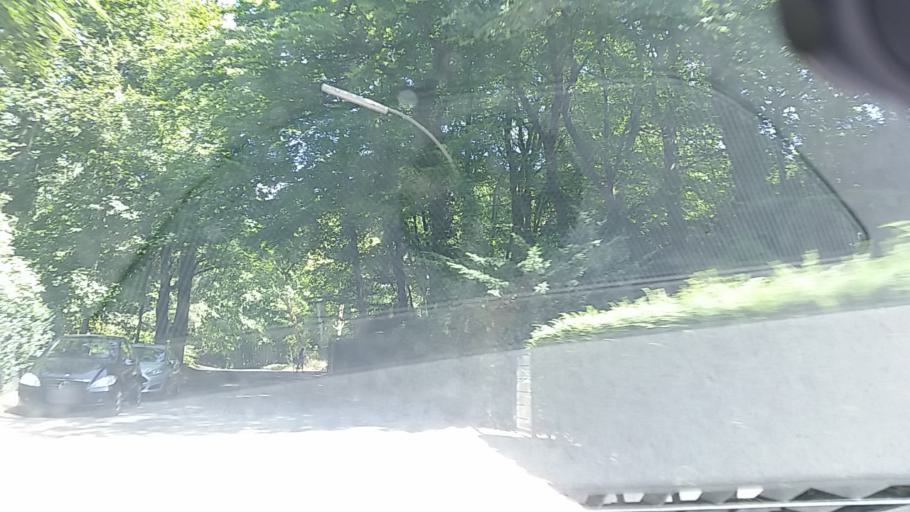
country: DE
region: Schleswig-Holstein
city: Wedel
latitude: 53.5674
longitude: 9.7718
